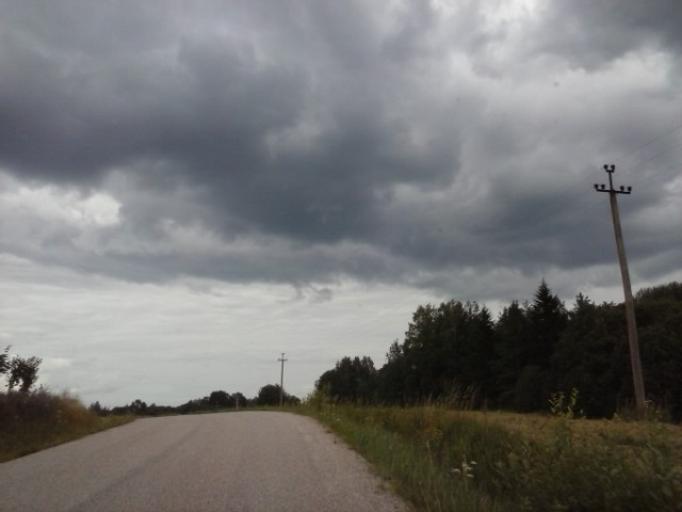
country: EE
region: Vorumaa
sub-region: Voru linn
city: Voru
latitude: 57.7425
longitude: 27.1111
